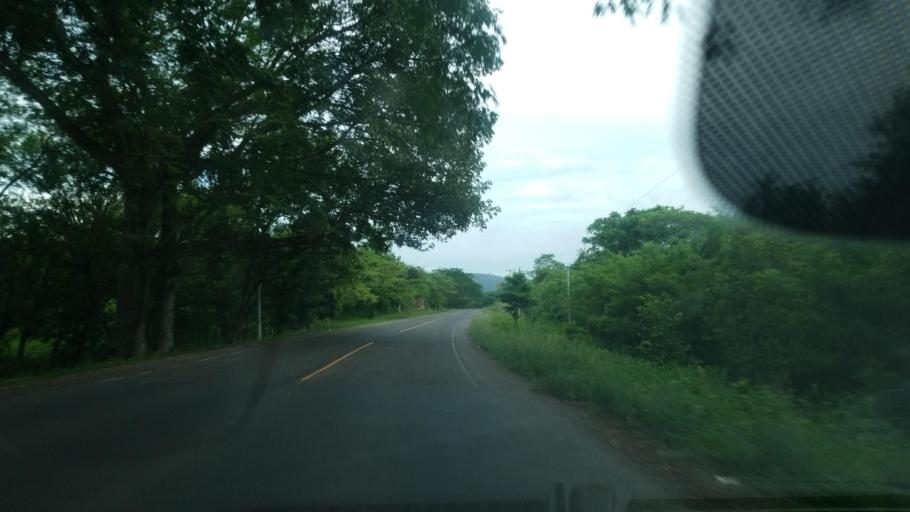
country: HN
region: Santa Barbara
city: Santa Barbara
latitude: 14.8898
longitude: -88.2488
